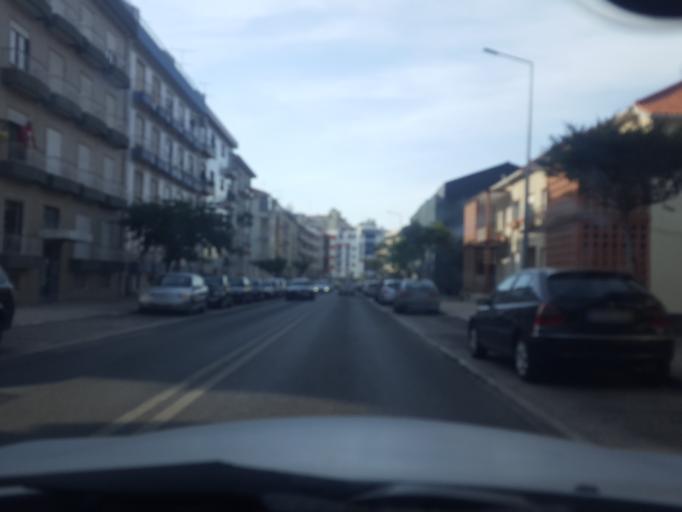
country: PT
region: Leiria
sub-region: Leiria
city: Leiria
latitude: 39.7379
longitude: -8.8009
